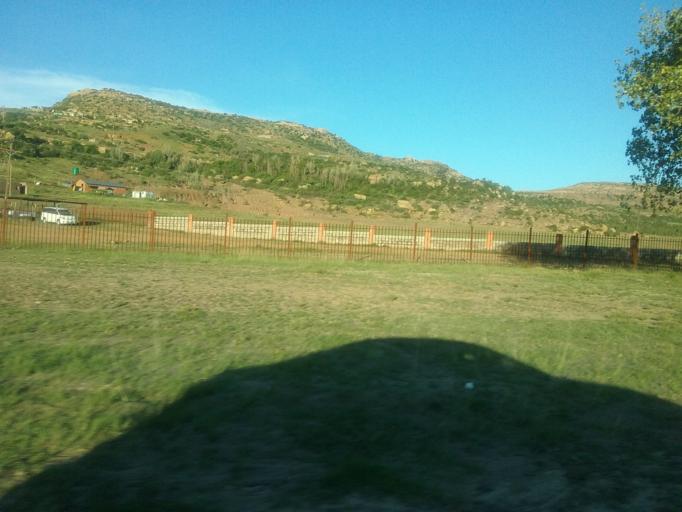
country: LS
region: Maseru
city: Maseru
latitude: -29.2591
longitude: 27.6024
